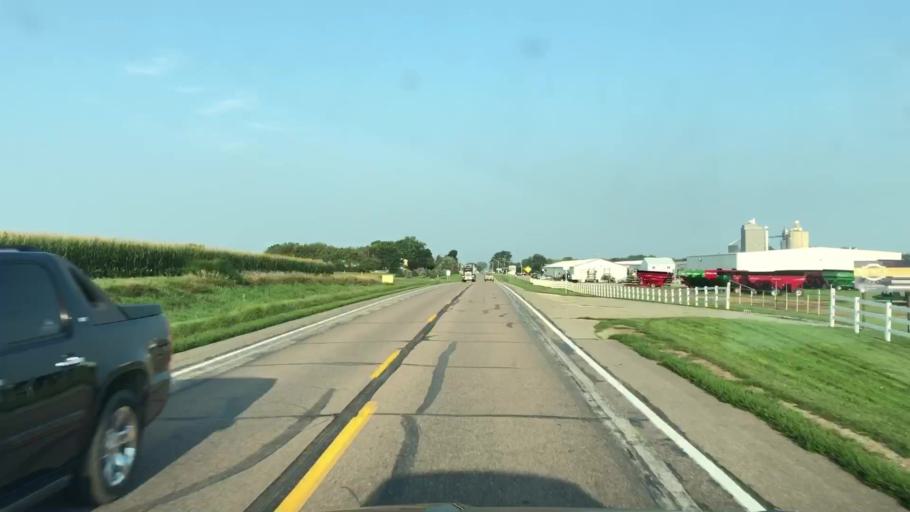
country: US
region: Iowa
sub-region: O'Brien County
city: Sheldon
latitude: 43.1862
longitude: -95.9917
